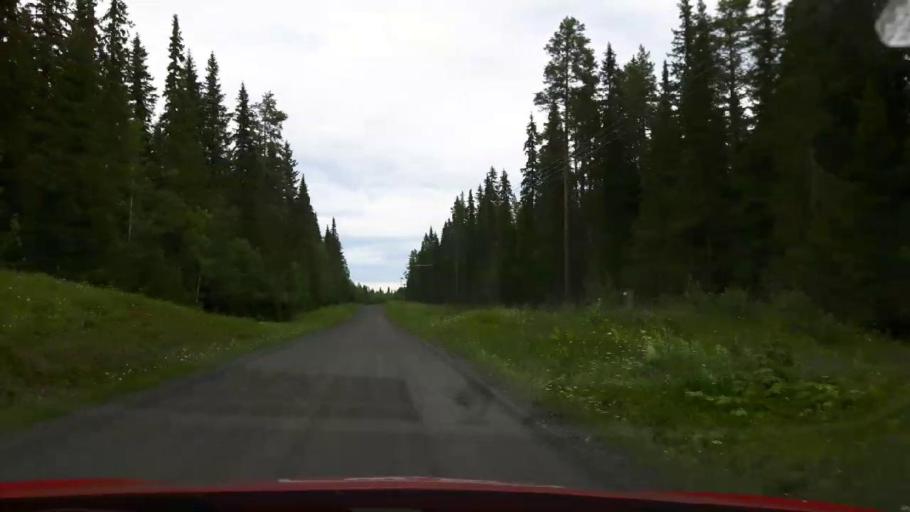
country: SE
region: Jaemtland
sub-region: Stroemsunds Kommun
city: Stroemsund
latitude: 63.4662
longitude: 15.2855
